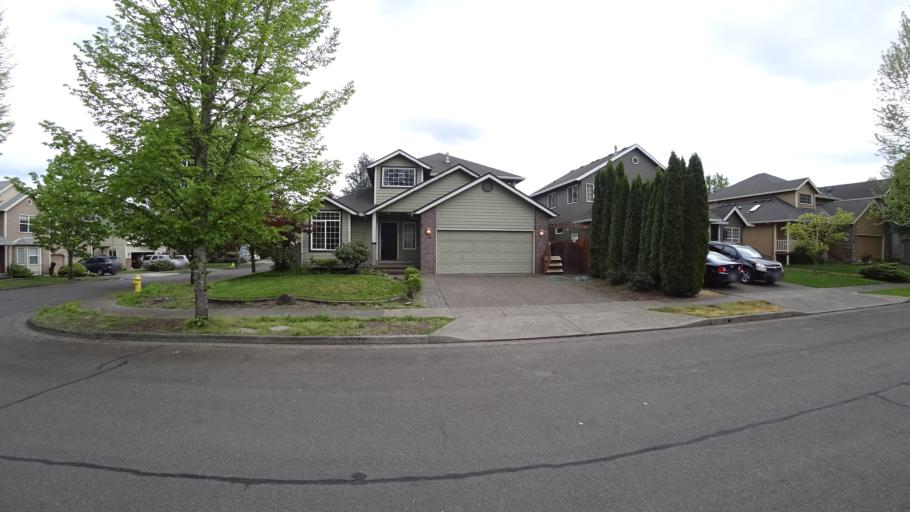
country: US
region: Oregon
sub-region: Washington County
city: Rockcreek
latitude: 45.5404
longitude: -122.9309
